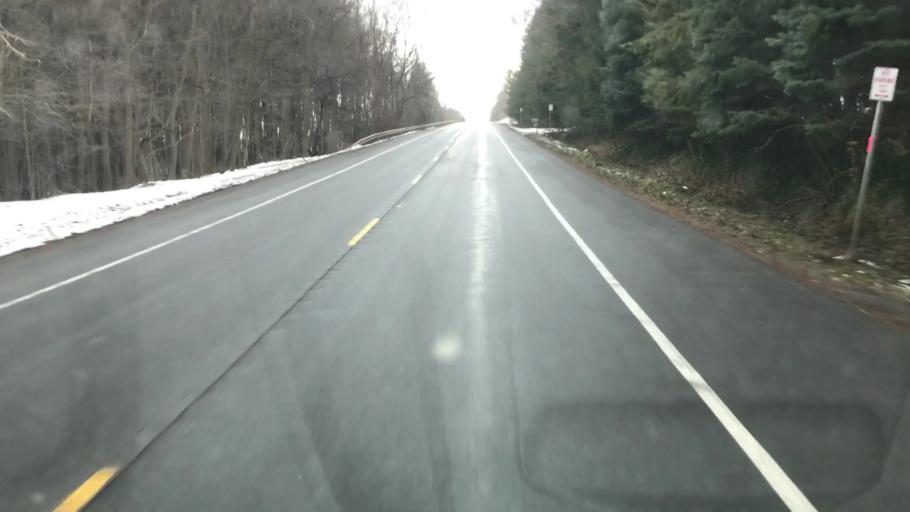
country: US
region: New York
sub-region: Onondaga County
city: Skaneateles
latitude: 42.9089
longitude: -76.4267
